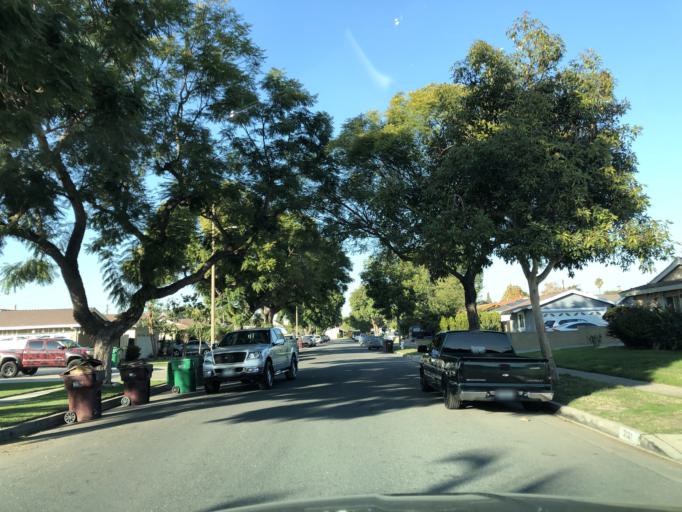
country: US
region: California
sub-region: Orange County
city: Santa Ana
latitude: 33.7640
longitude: -117.8543
